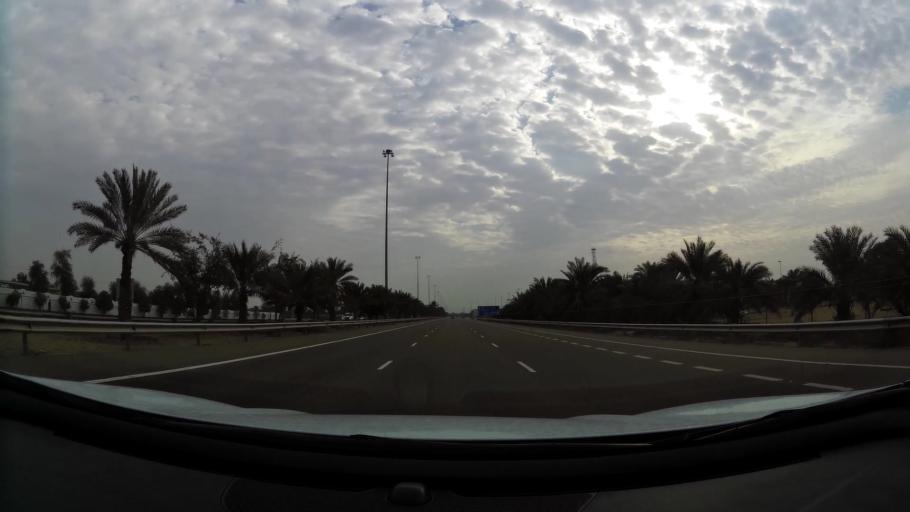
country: AE
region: Abu Dhabi
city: Al Ain
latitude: 24.1707
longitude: 55.1070
